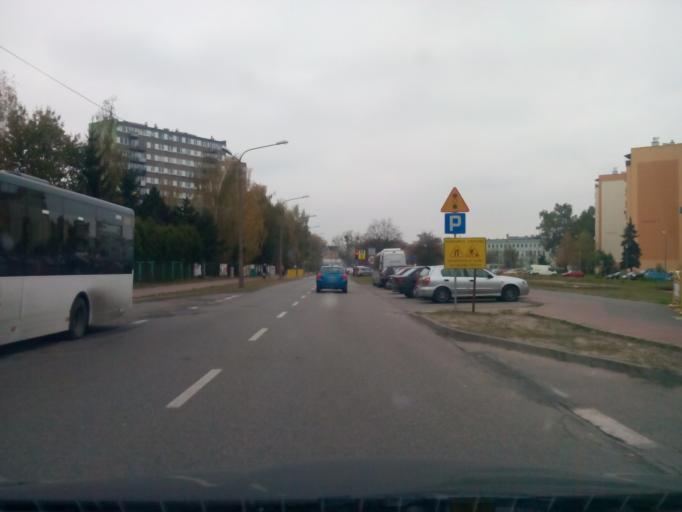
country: PL
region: Masovian Voivodeship
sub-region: Powiat pruszkowski
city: Pruszkow
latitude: 52.1570
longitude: 20.7935
